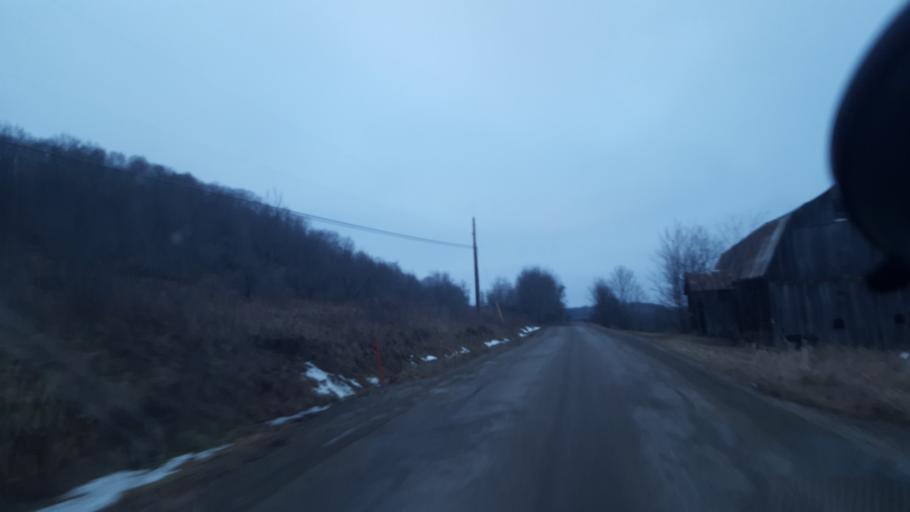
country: US
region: Pennsylvania
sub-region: Tioga County
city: Westfield
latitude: 41.9503
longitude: -77.6896
